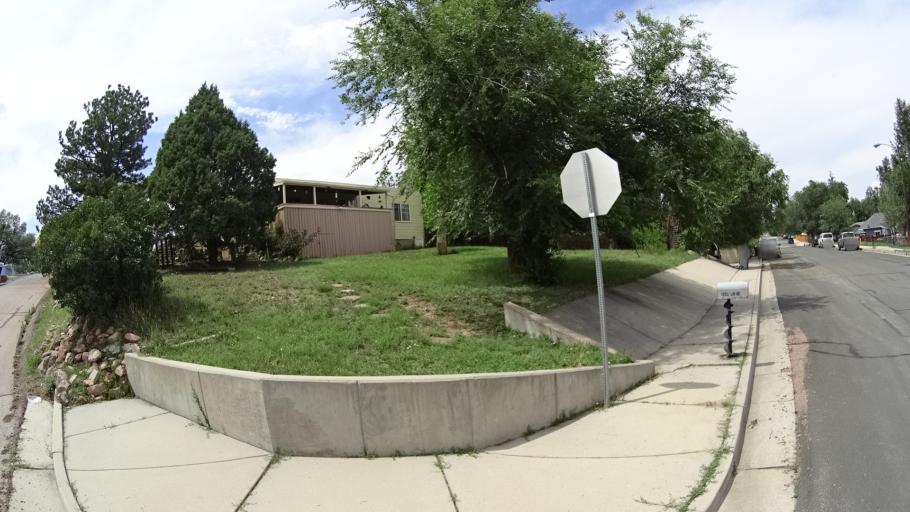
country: US
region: Colorado
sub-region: El Paso County
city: Colorado Springs
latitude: 38.8620
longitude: -104.8377
